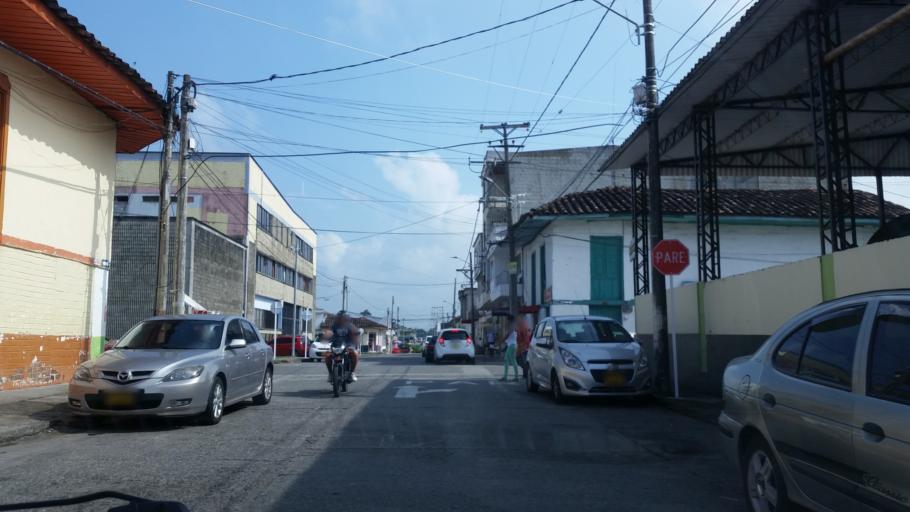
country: CO
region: Quindio
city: Quimbaya
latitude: 4.6222
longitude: -75.7602
